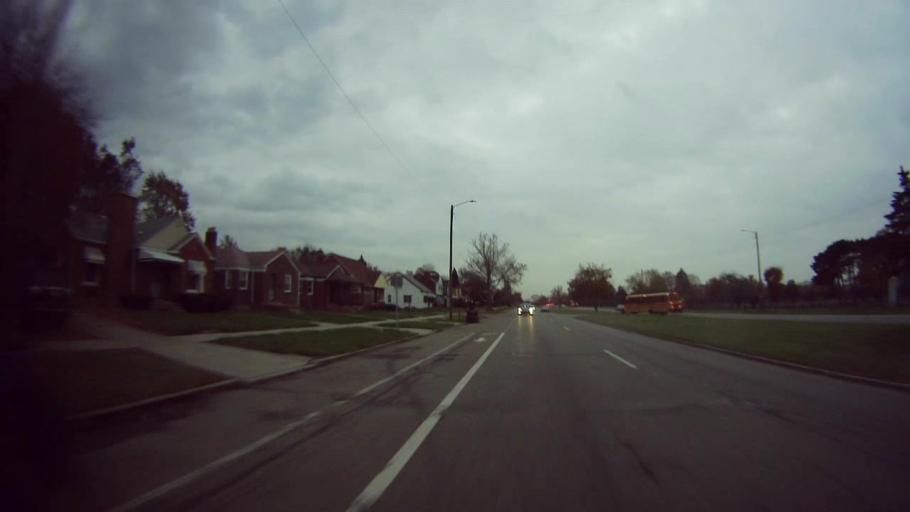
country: US
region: Michigan
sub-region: Macomb County
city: Warren
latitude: 42.4318
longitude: -83.0144
